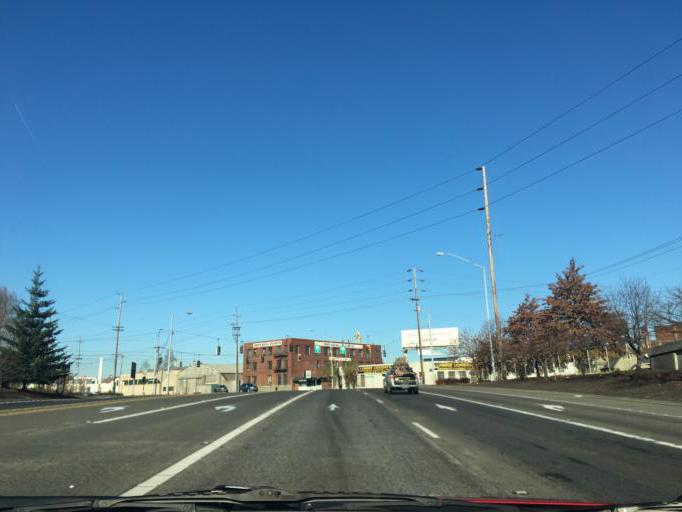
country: US
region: Oregon
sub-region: Multnomah County
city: Portland
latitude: 45.5400
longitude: -122.6984
